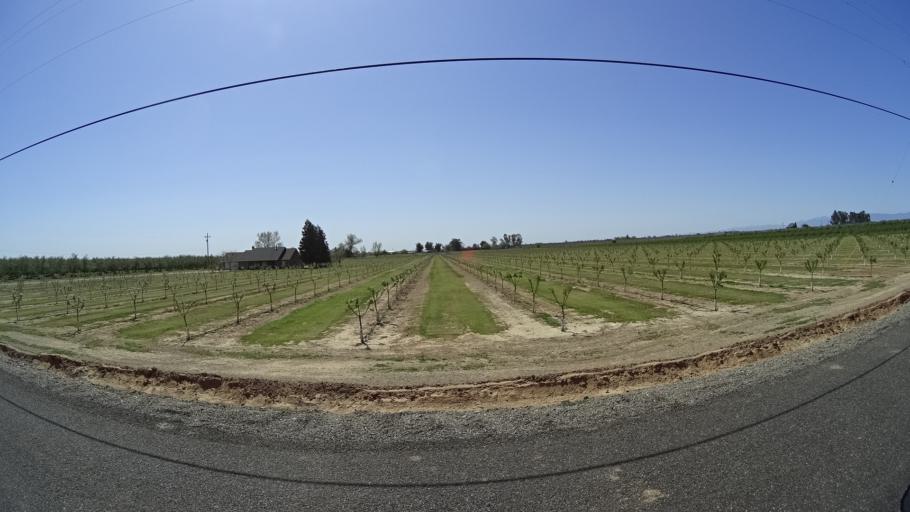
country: US
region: California
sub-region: Glenn County
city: Hamilton City
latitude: 39.7897
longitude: -122.0979
